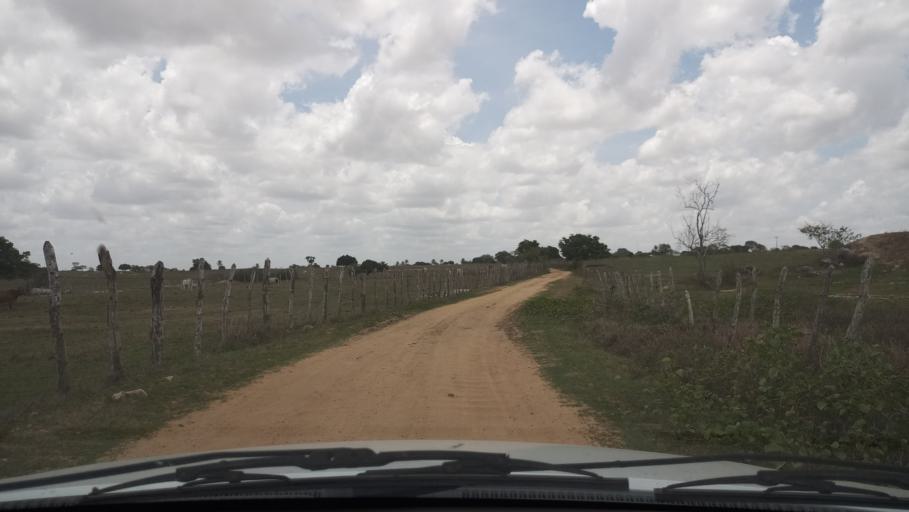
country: BR
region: Rio Grande do Norte
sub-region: Brejinho
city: Brejinho
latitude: -6.2739
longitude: -35.3390
